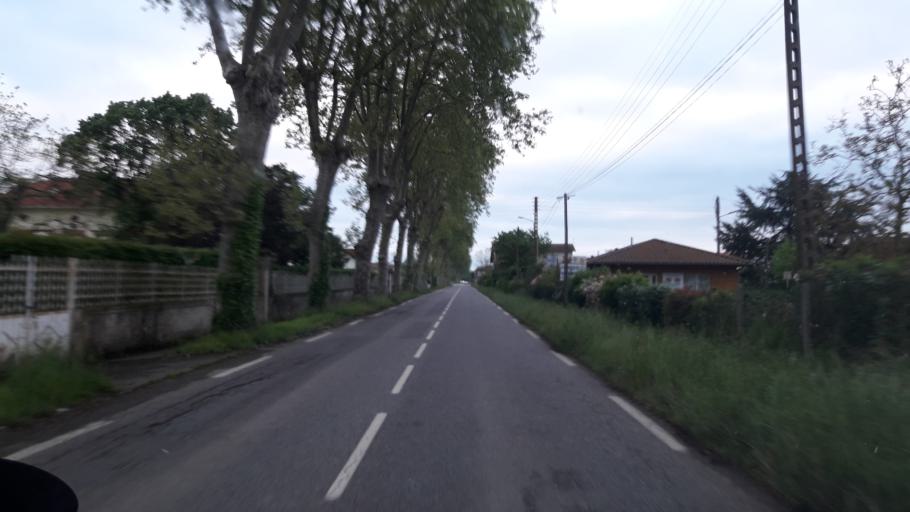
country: FR
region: Midi-Pyrenees
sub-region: Departement de la Haute-Garonne
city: Cazeres
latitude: 43.2153
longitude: 1.0853
